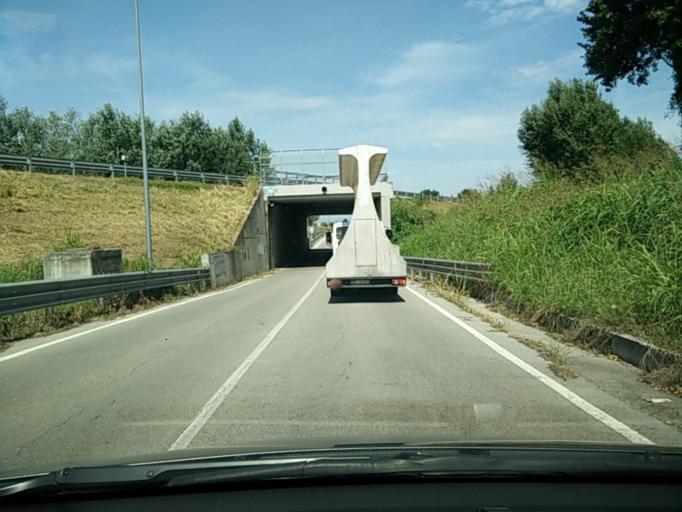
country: IT
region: Veneto
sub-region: Provincia di Venezia
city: Passarella
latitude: 45.5988
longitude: 12.5942
